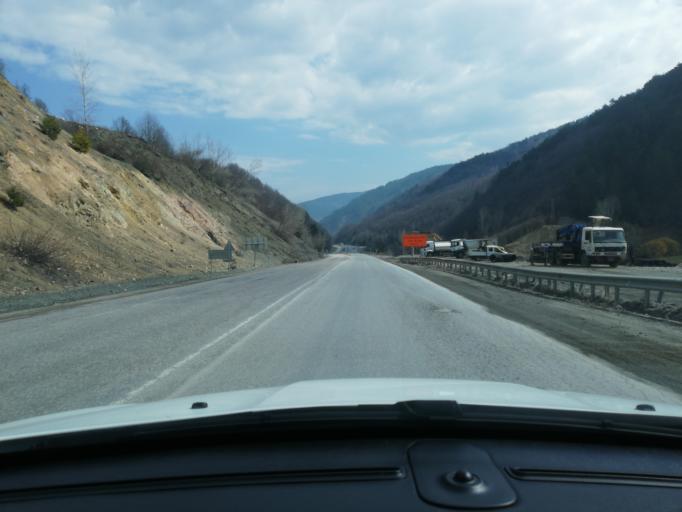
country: TR
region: Kastamonu
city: Kuzyaka
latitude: 41.1133
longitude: 33.7475
